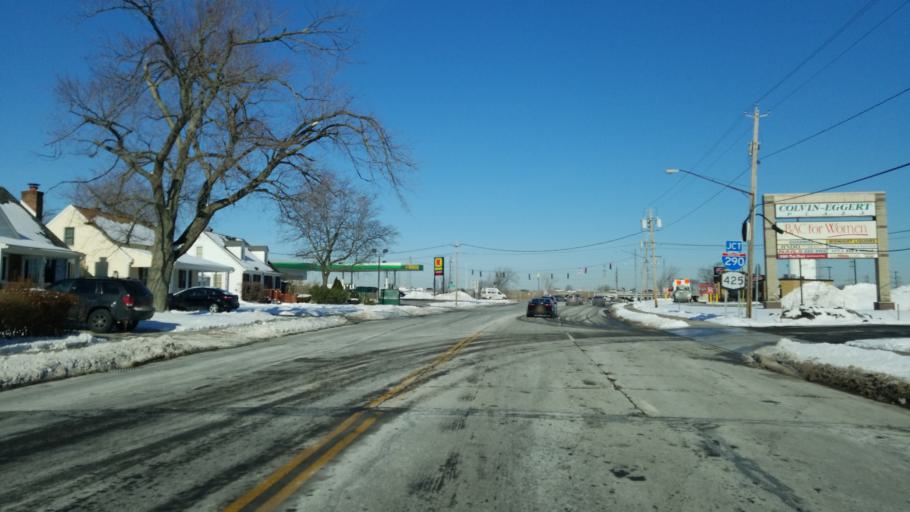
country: US
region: New York
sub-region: Erie County
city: Tonawanda
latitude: 42.9973
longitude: -78.8506
